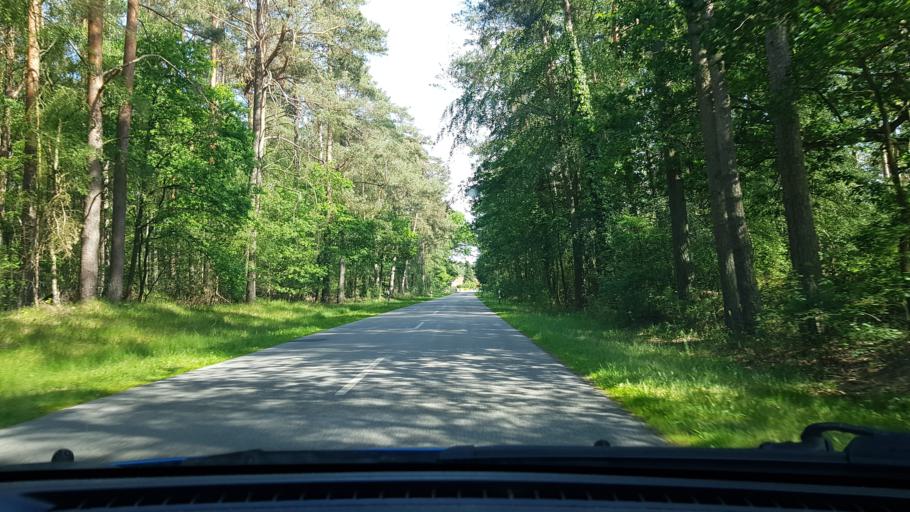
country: DE
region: Lower Saxony
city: Neu Darchau
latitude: 53.3089
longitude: 10.9188
